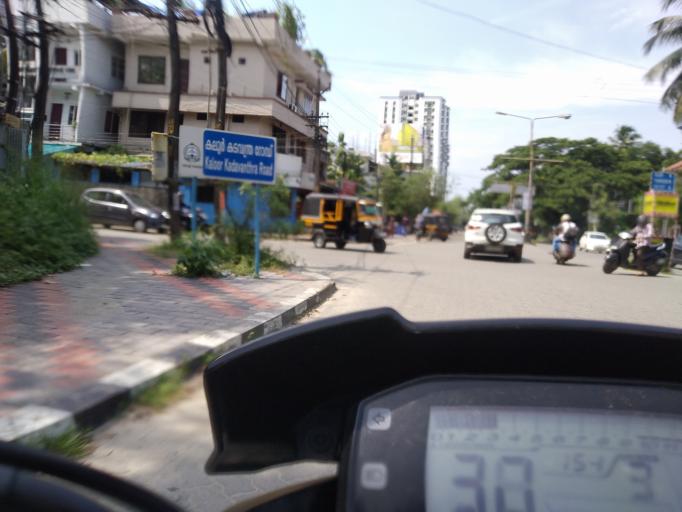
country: IN
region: Kerala
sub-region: Ernakulam
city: Cochin
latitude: 9.9725
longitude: 76.2982
